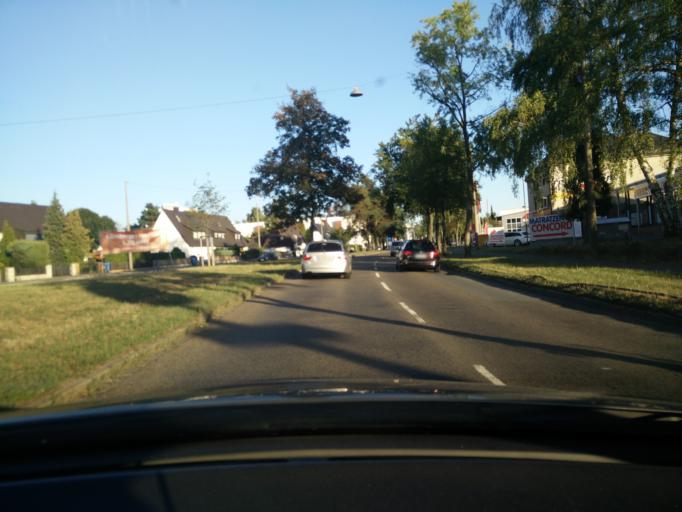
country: DE
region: Bavaria
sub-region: Regierungsbezirk Mittelfranken
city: Wendelstein
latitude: 49.4032
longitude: 11.1165
